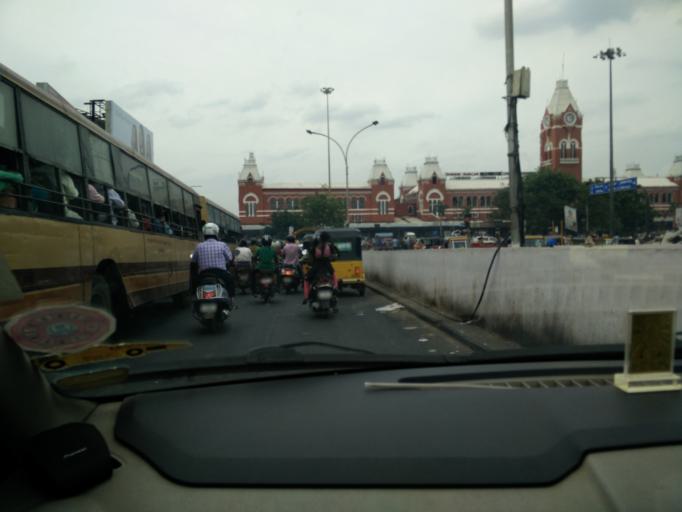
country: IN
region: Tamil Nadu
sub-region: Chennai
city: Chennai
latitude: 13.0811
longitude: 80.2752
